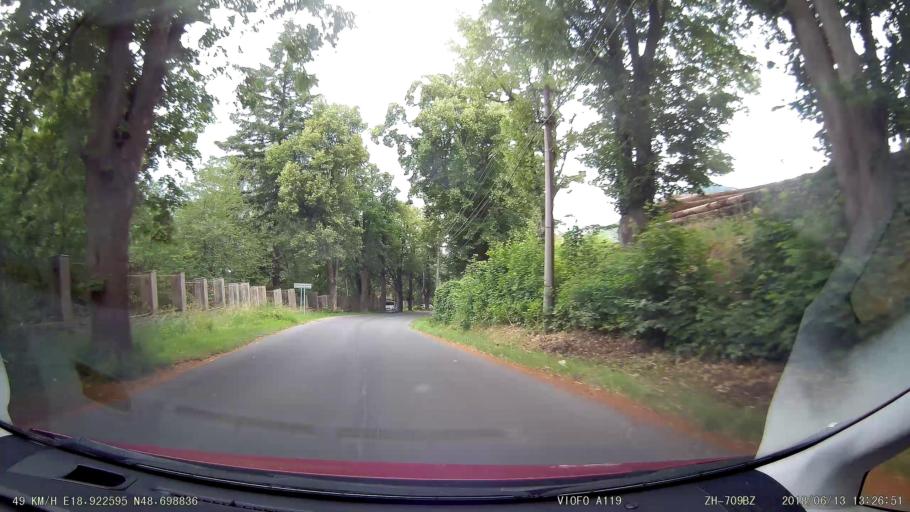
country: SK
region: Banskobystricky
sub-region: Okres Ziar nad Hronom
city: Kremnica
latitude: 48.6990
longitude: 18.9226
